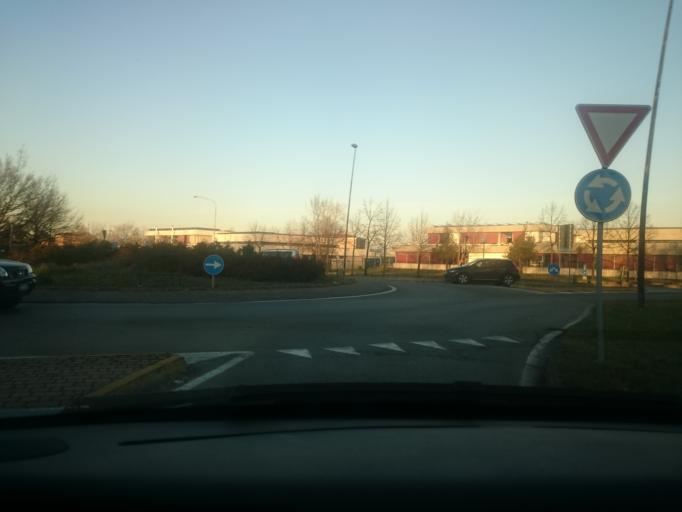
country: IT
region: Emilia-Romagna
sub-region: Provincia di Reggio Emilia
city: Scandiano
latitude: 44.5947
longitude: 10.6999
